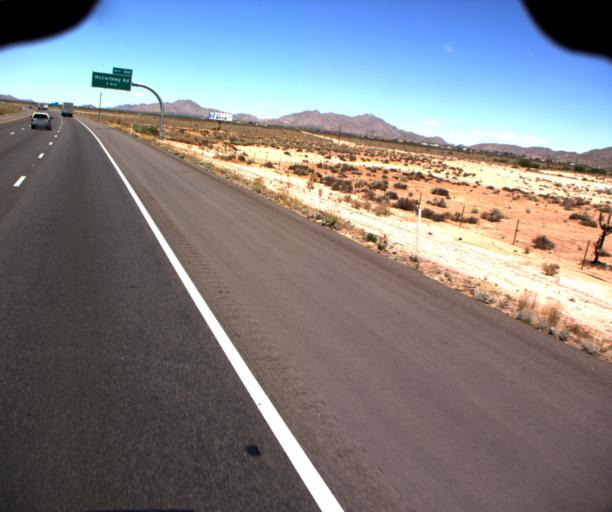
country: US
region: Arizona
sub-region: Pinal County
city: Casa Grande
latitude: 32.9204
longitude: -111.6882
